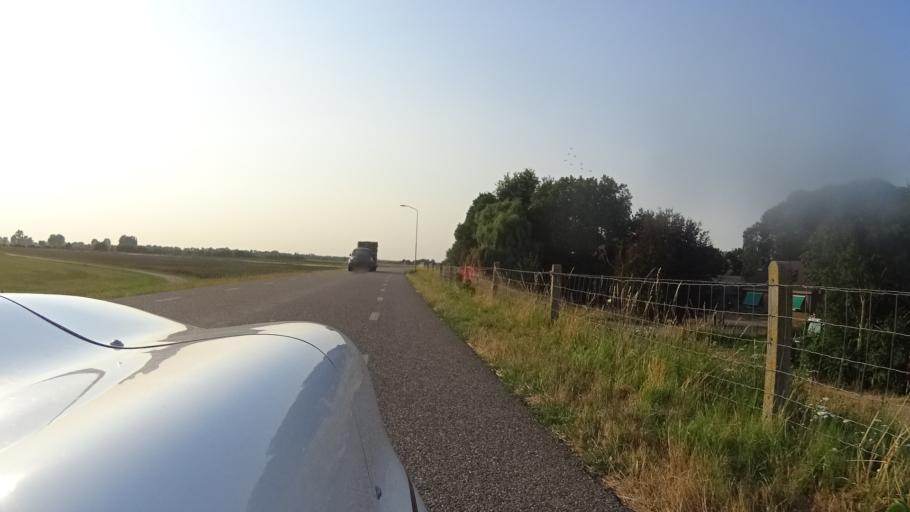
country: NL
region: Gelderland
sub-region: Gemeente Wijchen
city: Bergharen
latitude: 51.8137
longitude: 5.6561
